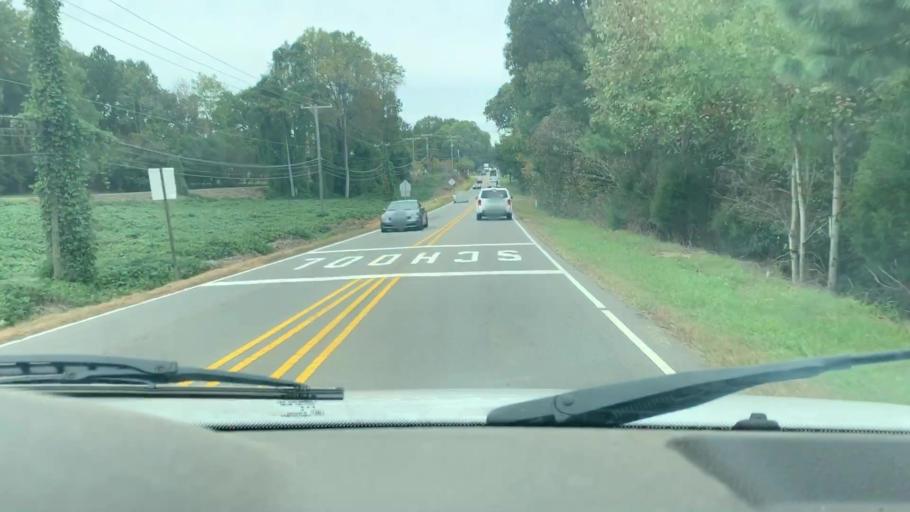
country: US
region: North Carolina
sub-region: Gaston County
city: Davidson
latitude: 35.5490
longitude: -80.8455
